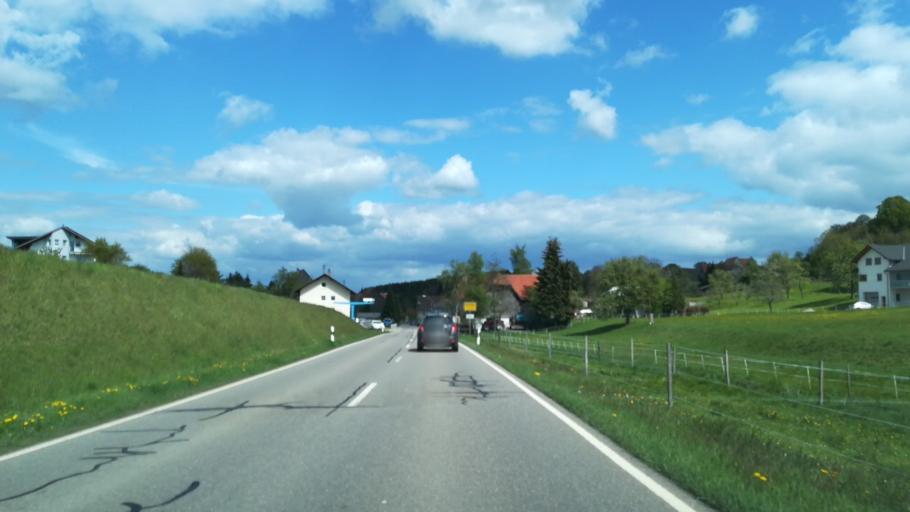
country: DE
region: Baden-Wuerttemberg
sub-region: Freiburg Region
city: Bonndorf im Schwarzwald
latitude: 47.8246
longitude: 8.3915
